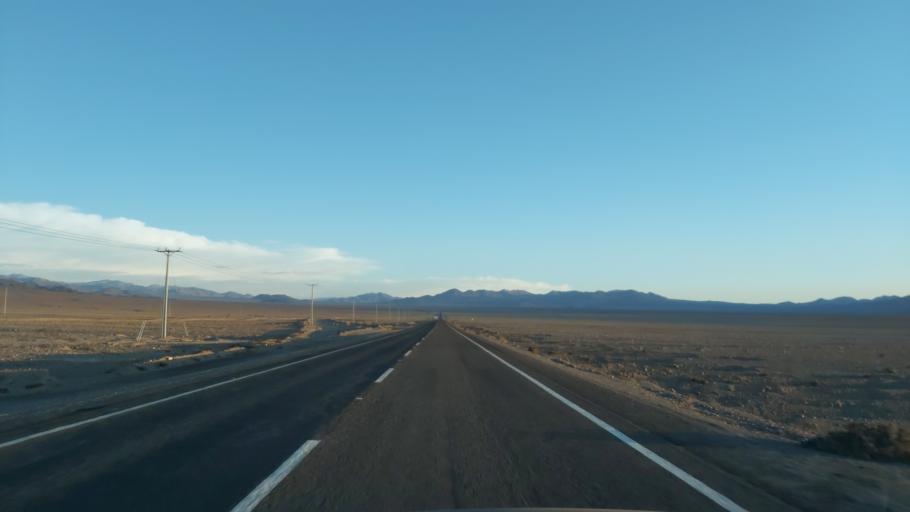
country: CL
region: Atacama
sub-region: Provincia de Chanaral
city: Diego de Almagro
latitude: -26.6180
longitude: -69.9523
